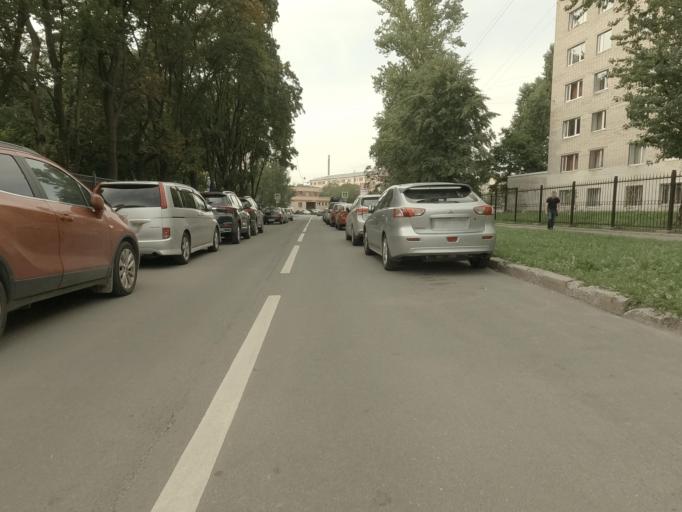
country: RU
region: St.-Petersburg
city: Admiralteisky
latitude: 59.9049
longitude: 30.2689
